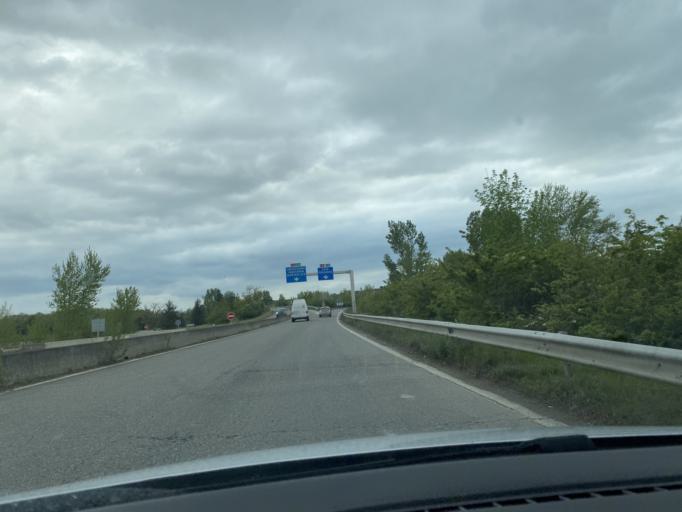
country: FR
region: Midi-Pyrenees
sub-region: Departement de la Haute-Garonne
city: Gardouch
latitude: 43.3980
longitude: 1.6954
